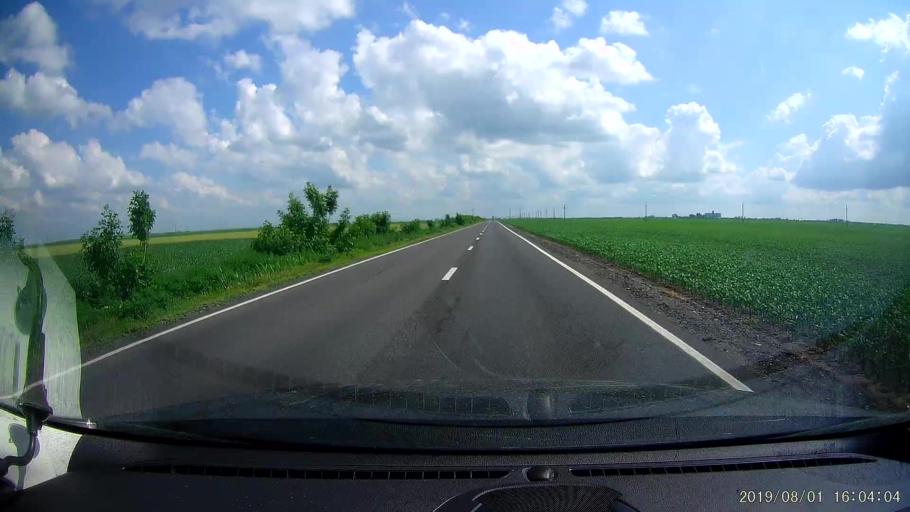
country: RO
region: Calarasi
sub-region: Comuna Dragalina
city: Drajna Noua
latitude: 44.4574
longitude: 27.3818
